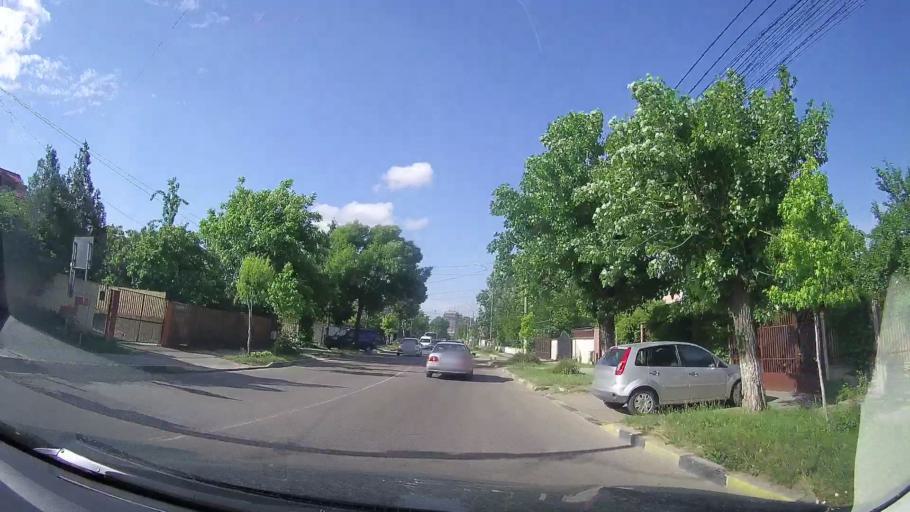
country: RO
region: Ilfov
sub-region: Comuna Magurele
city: Magurele
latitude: 44.3556
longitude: 26.0344
